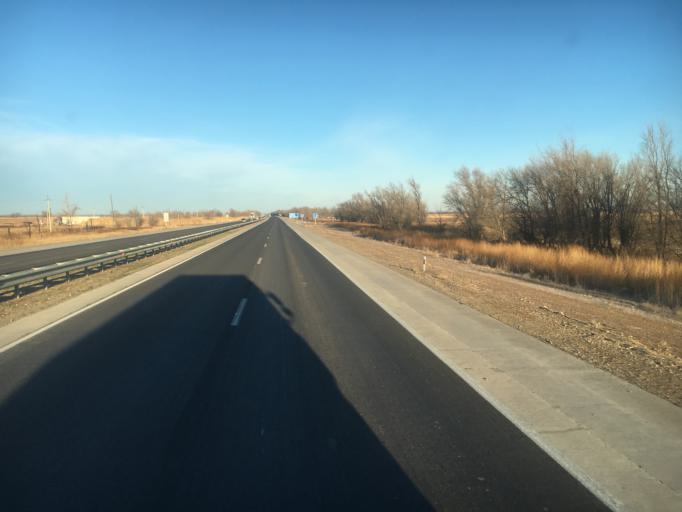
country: KZ
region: Ongtustik Qazaqstan
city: Bayaldyr
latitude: 43.0925
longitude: 68.6380
